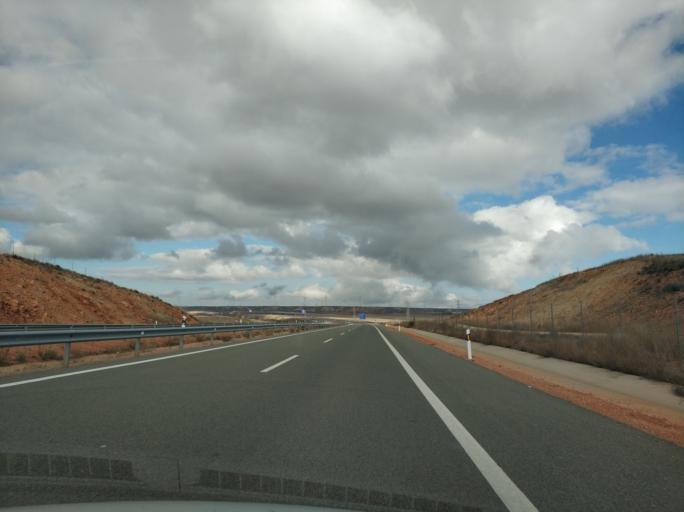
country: ES
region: Castille and Leon
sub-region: Provincia de Soria
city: Yelo
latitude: 41.2432
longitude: -2.4775
